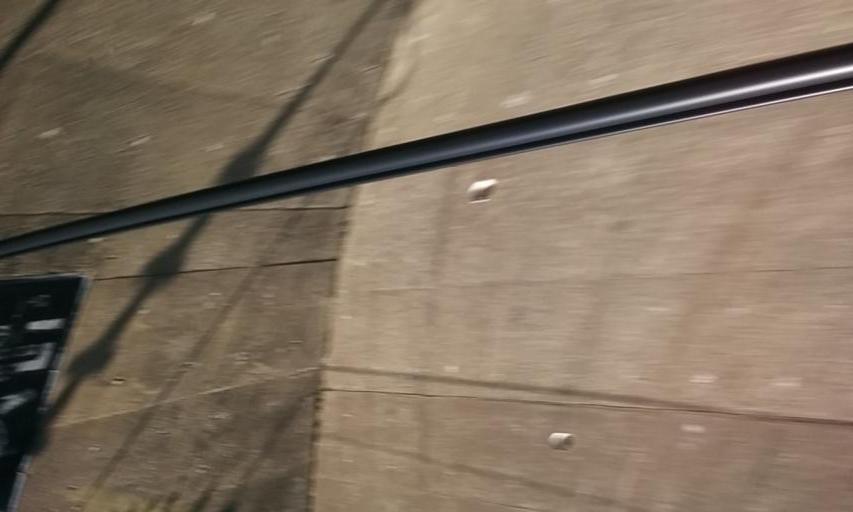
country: JP
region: Fukushima
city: Sukagawa
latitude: 37.2438
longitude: 140.2971
